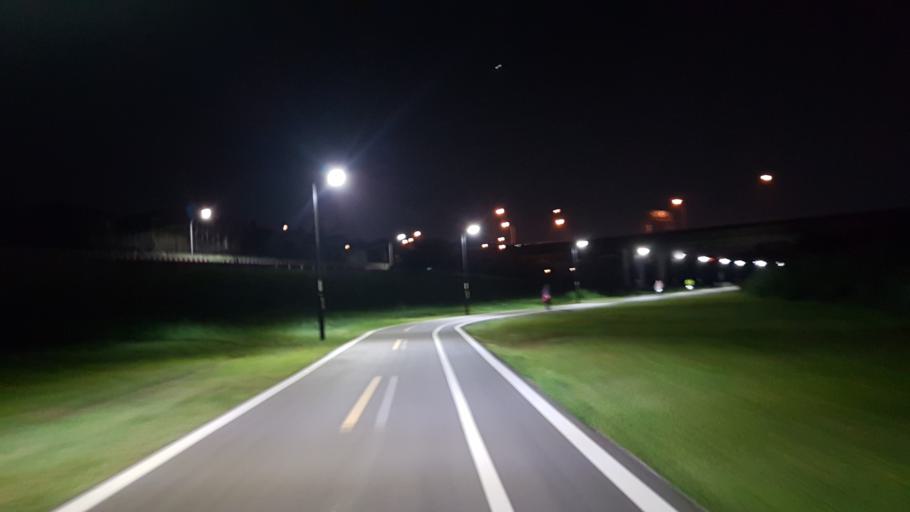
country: TW
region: Taipei
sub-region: Taipei
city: Banqiao
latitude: 24.9691
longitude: 121.5282
